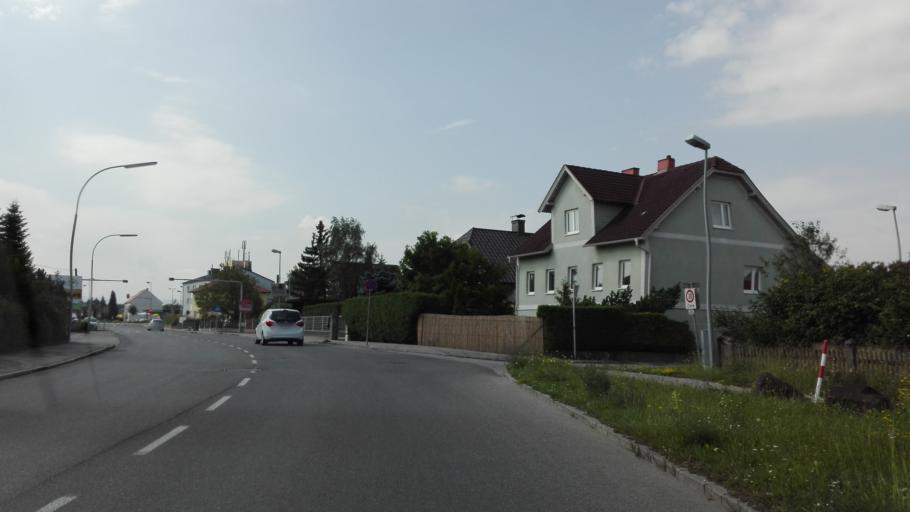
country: AT
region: Lower Austria
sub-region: Sankt Polten Stadt
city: Sankt Poelten
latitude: 48.1725
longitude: 15.6145
